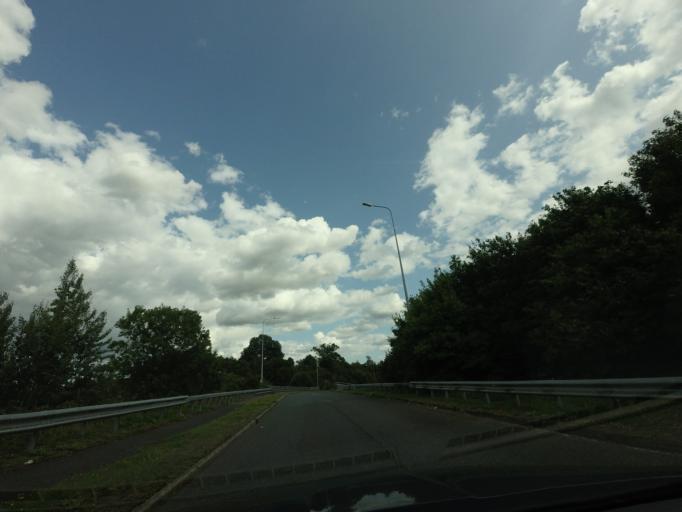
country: GB
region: England
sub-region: Kent
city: Harrietsham
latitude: 51.2618
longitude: 0.6115
